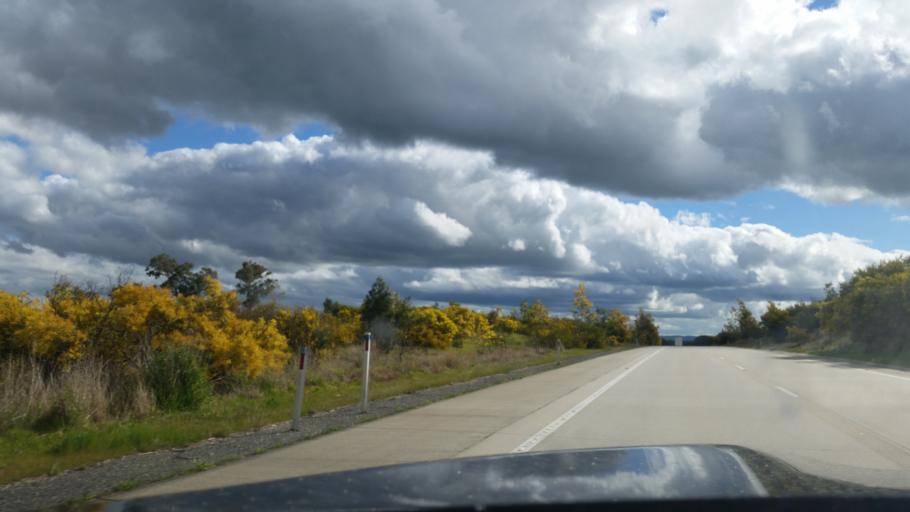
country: AU
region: New South Wales
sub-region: Greater Hume Shire
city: Jindera
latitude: -35.9243
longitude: 147.0537
